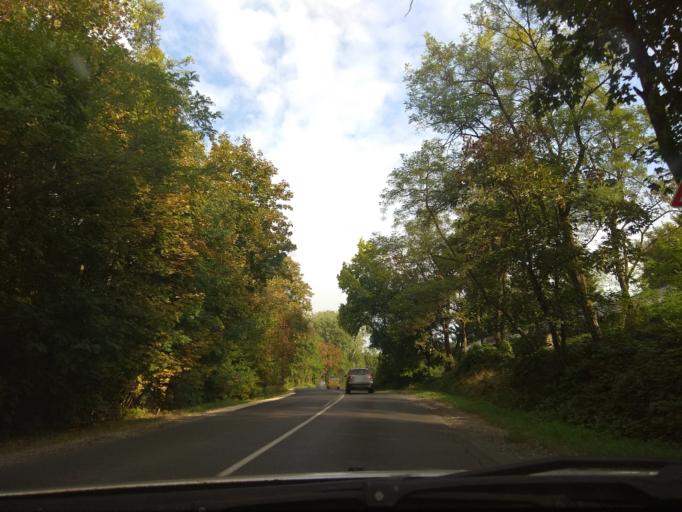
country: HU
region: Borsod-Abauj-Zemplen
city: Miskolc
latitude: 48.0798
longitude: 20.7718
